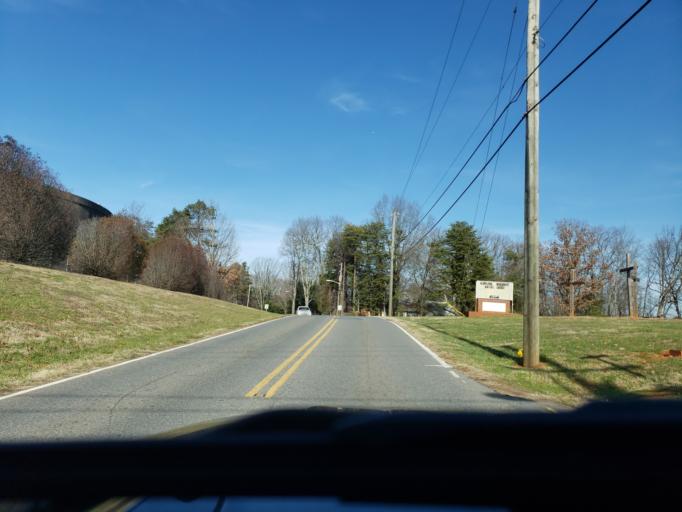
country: US
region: North Carolina
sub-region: Cleveland County
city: Kings Mountain
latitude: 35.2589
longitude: -81.3367
